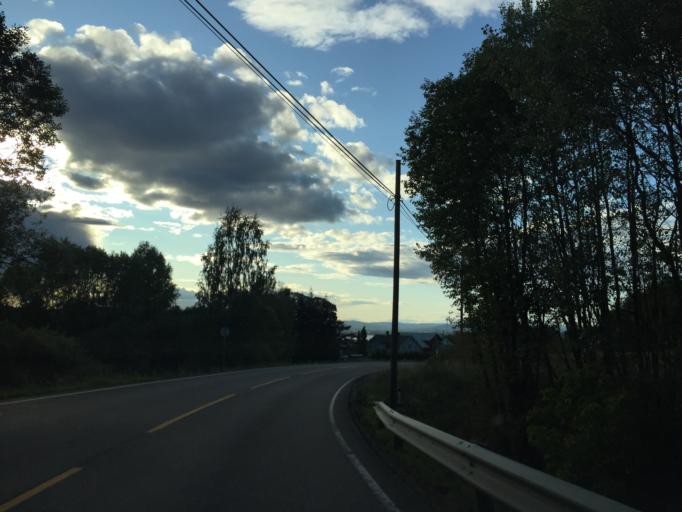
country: NO
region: Akershus
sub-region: Fet
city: Fetsund
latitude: 59.9006
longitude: 11.1863
